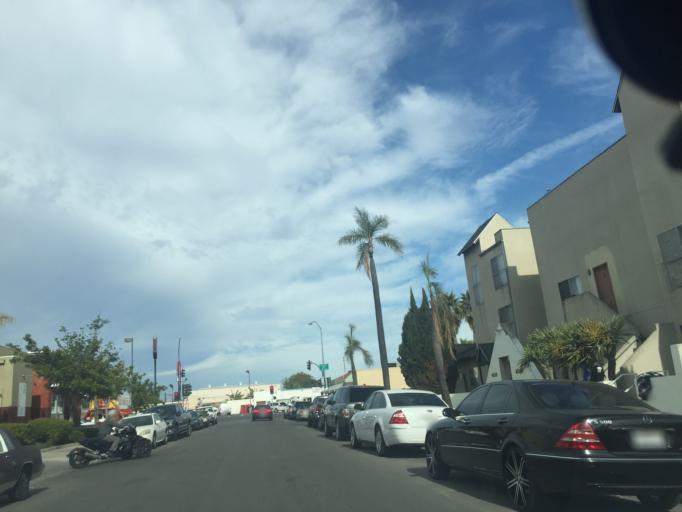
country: US
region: California
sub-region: San Diego County
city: Lemon Grove
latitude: 32.7547
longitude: -117.0965
